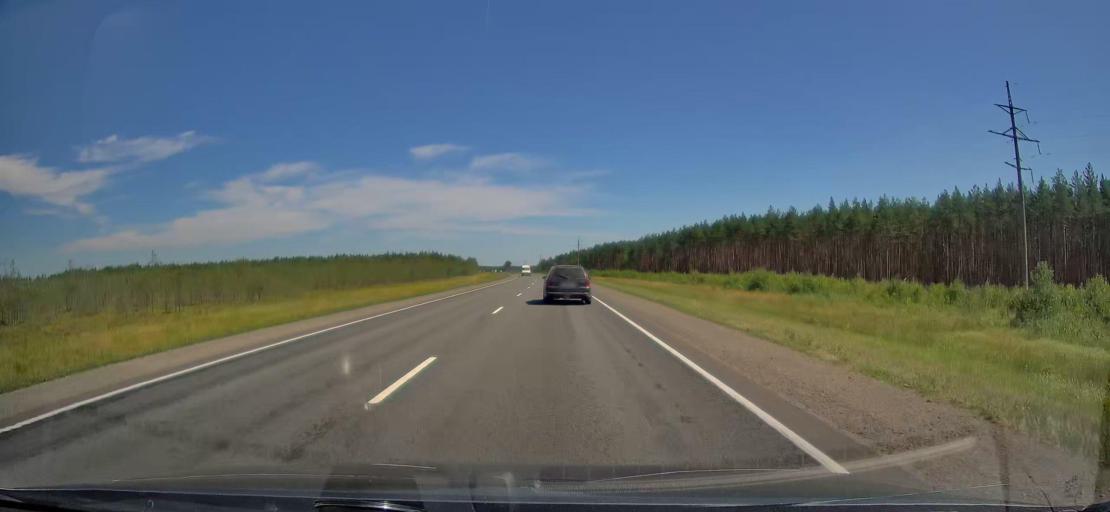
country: RU
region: Vologda
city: Khokhlovo
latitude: 58.9305
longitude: 37.2605
